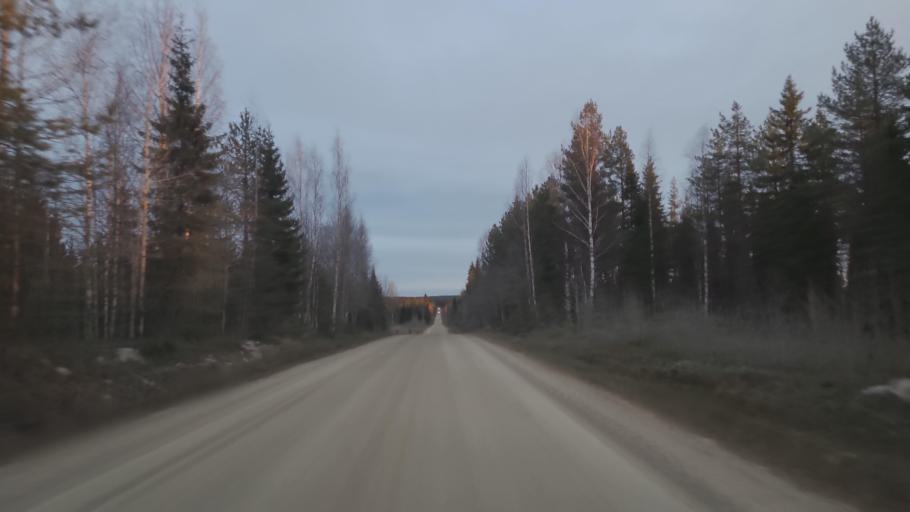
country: FI
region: Lapland
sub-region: Kemi-Tornio
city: Tervola
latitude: 66.0571
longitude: 24.9474
